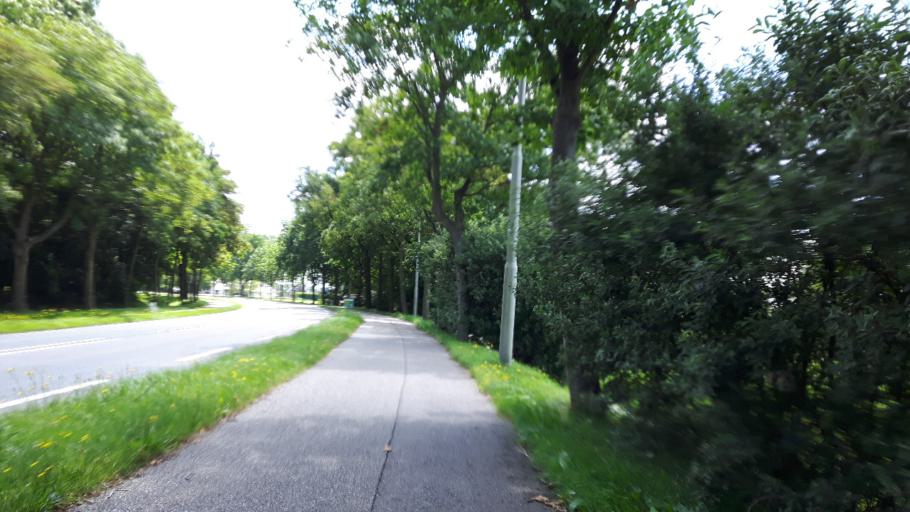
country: NL
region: Utrecht
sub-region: Stichtse Vecht
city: Vreeland
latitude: 52.2180
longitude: 5.0098
